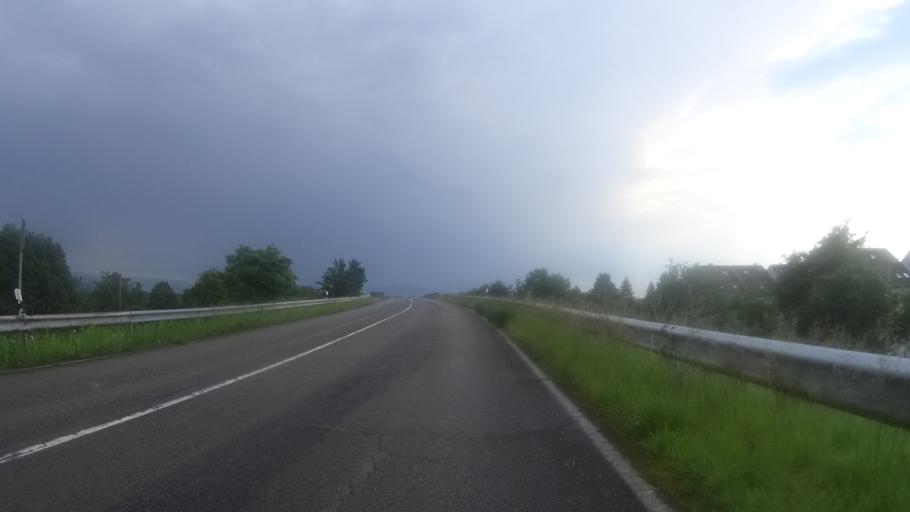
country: DE
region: Baden-Wuerttemberg
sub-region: Karlsruhe Region
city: Bietigheim
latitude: 48.9005
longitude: 8.2492
